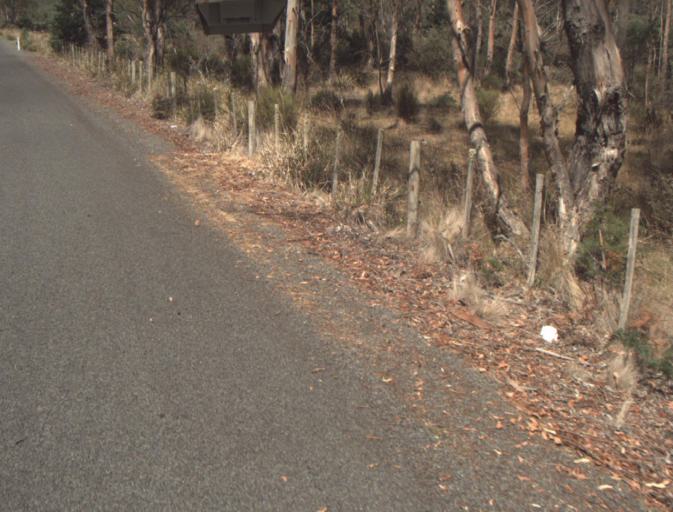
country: AU
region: Tasmania
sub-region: Launceston
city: Newstead
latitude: -41.3714
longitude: 147.2982
